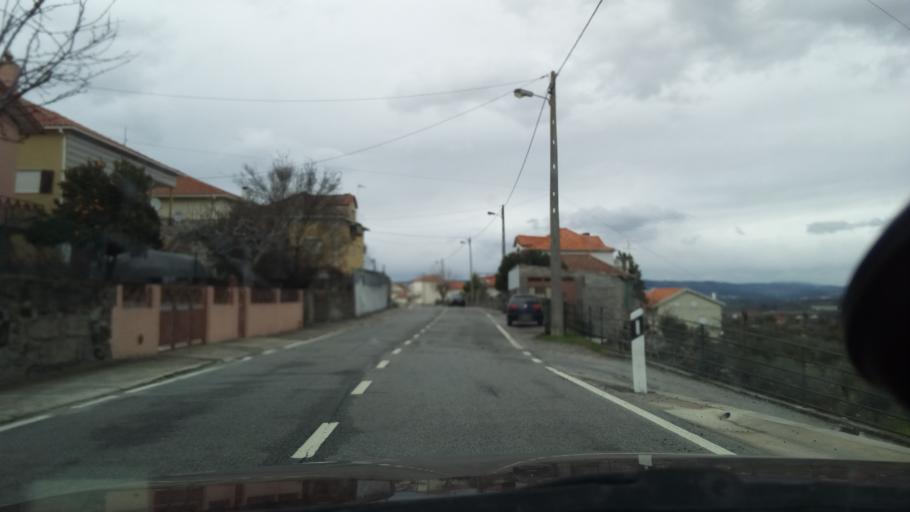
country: PT
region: Guarda
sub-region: Fornos de Algodres
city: Fornos de Algodres
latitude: 40.5199
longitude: -7.5803
